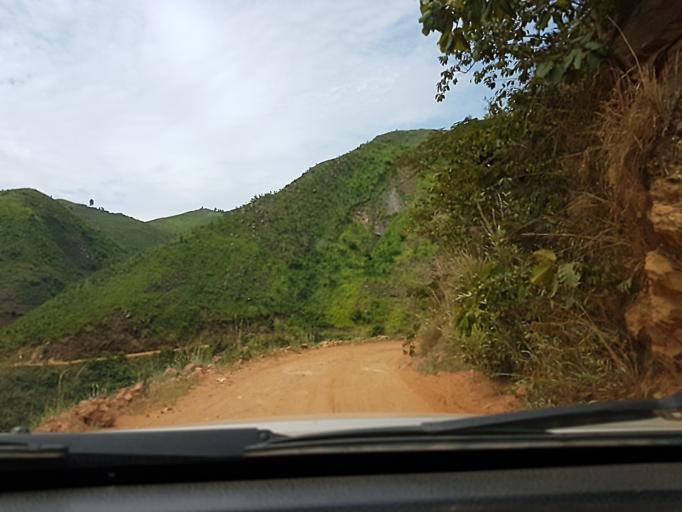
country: RW
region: Western Province
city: Cyangugu
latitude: -2.7066
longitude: 28.9448
